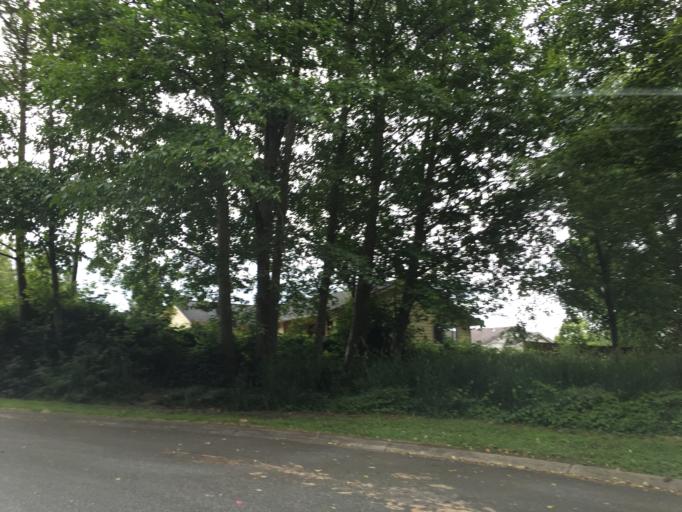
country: US
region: Washington
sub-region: Whatcom County
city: Birch Bay
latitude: 48.9488
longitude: -122.7378
